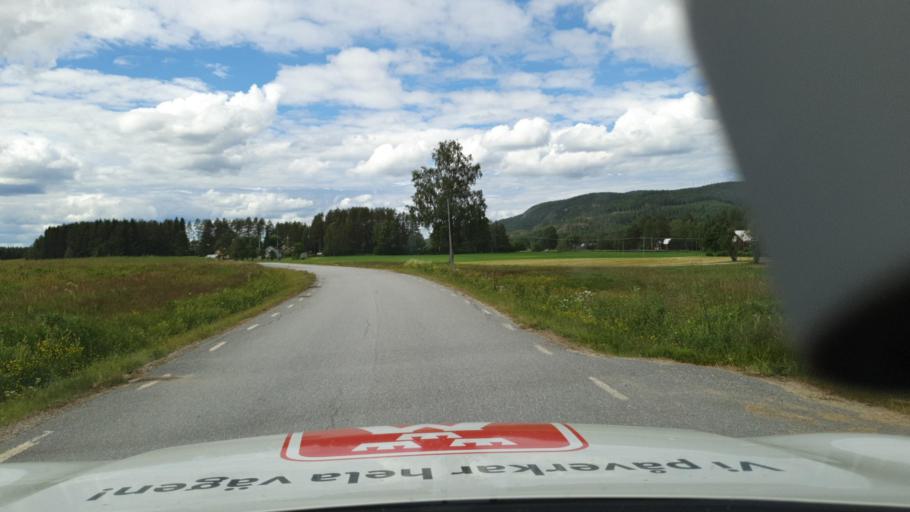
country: SE
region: Vaesterbotten
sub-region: Bjurholms Kommun
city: Bjurholm
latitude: 63.9154
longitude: 19.0763
